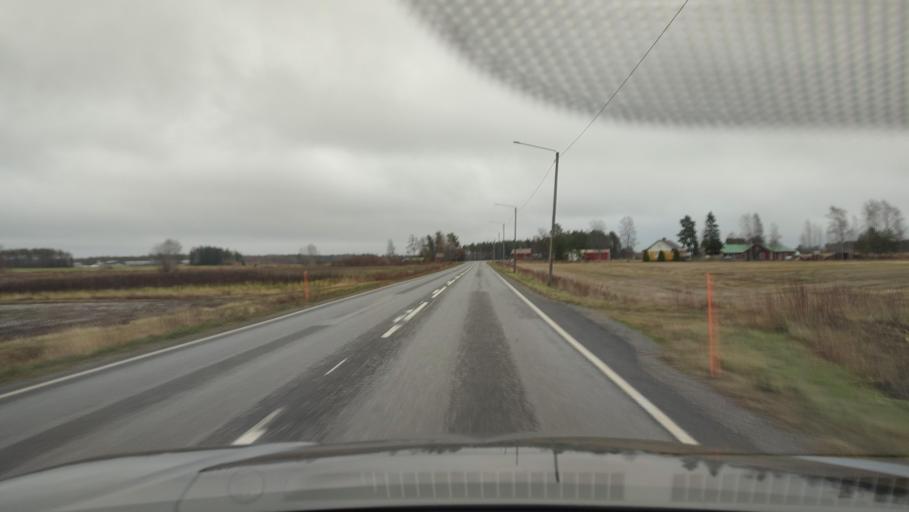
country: FI
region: Southern Ostrobothnia
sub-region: Suupohja
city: Isojoki
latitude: 62.1811
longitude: 21.8252
